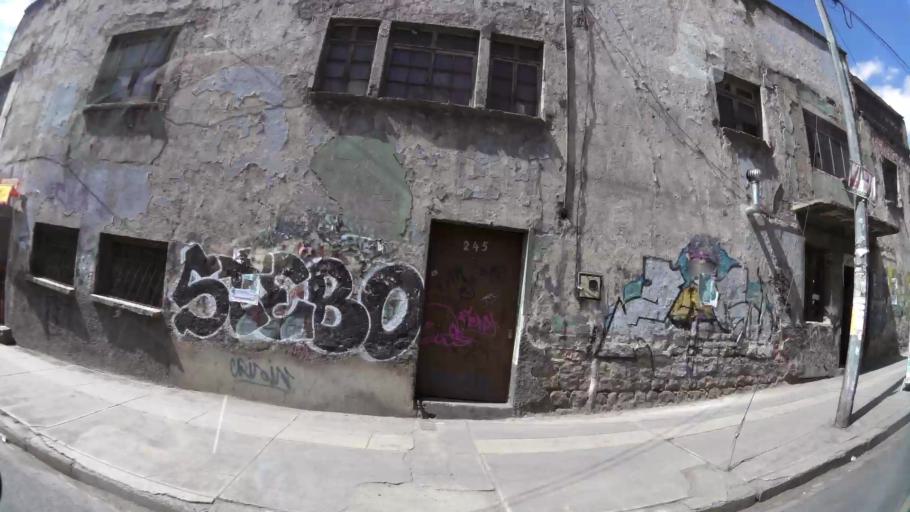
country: BO
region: La Paz
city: La Paz
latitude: -16.4898
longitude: -68.1443
